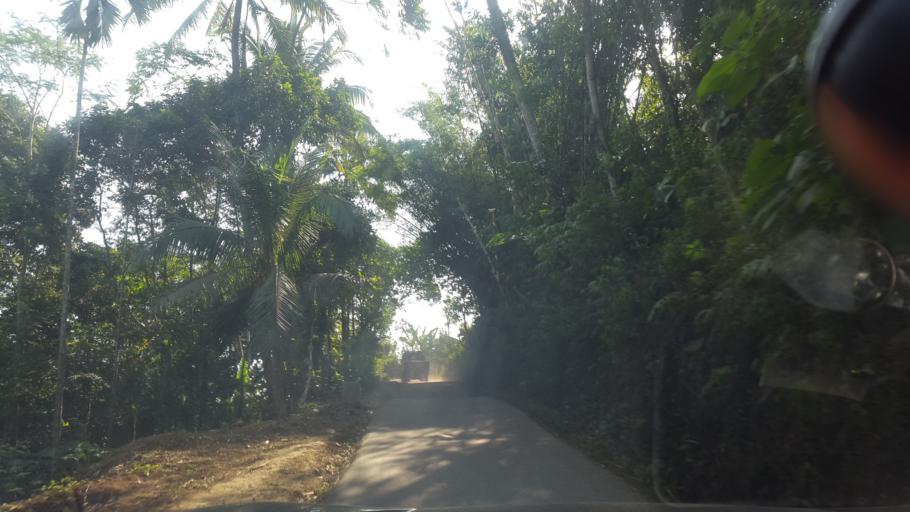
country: ID
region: West Java
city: Cicurug
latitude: -6.8803
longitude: 106.8215
